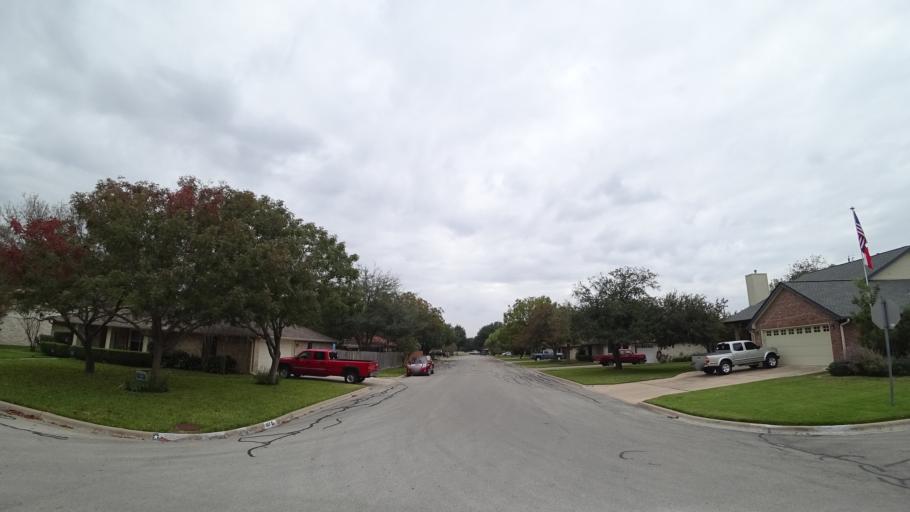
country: US
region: Texas
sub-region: Travis County
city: Pflugerville
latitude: 30.4518
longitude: -97.6222
